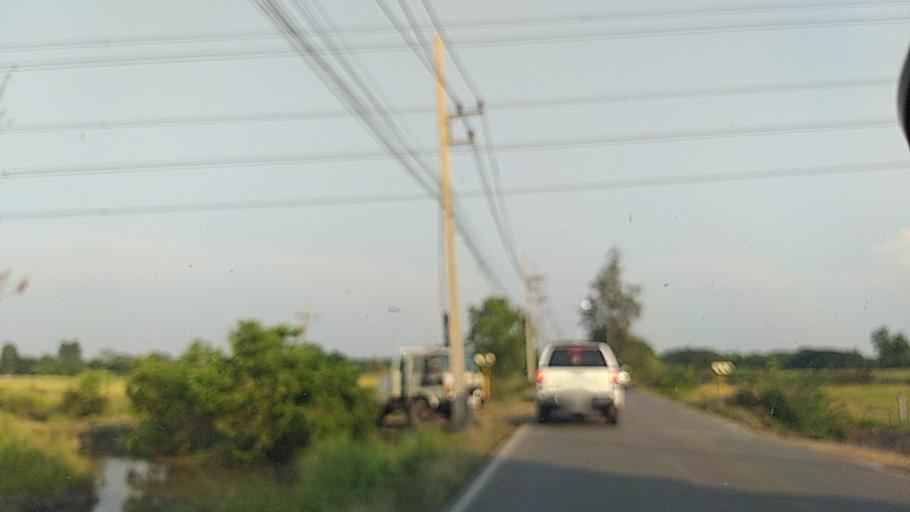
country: TH
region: Sara Buri
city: Nong Khae
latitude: 14.2805
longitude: 100.8178
